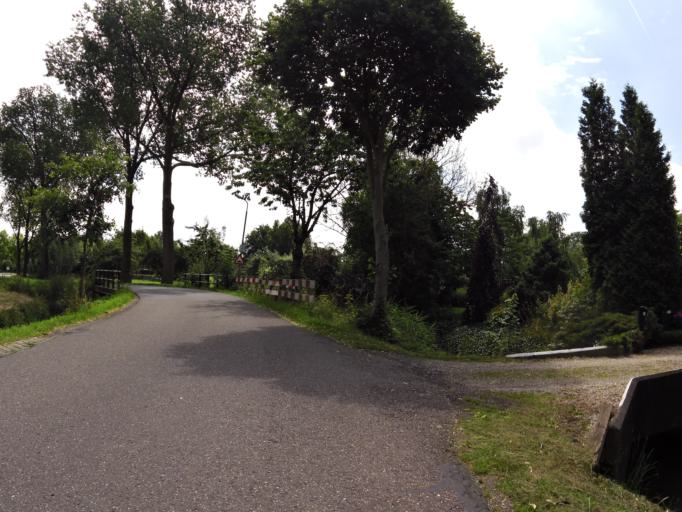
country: NL
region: South Holland
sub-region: Gemeente Leerdam
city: Leerdam
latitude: 51.9007
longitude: 5.0787
